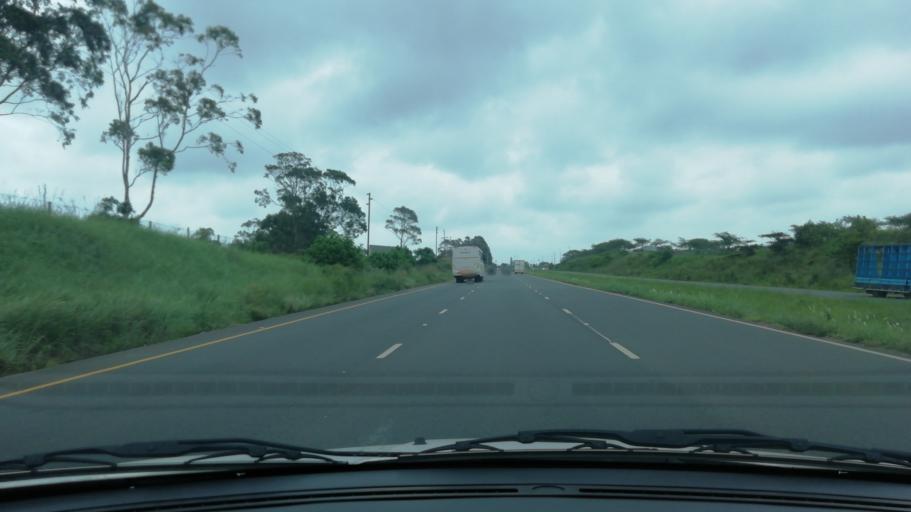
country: ZA
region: KwaZulu-Natal
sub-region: uThungulu District Municipality
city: Empangeni
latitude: -28.7669
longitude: 31.9198
